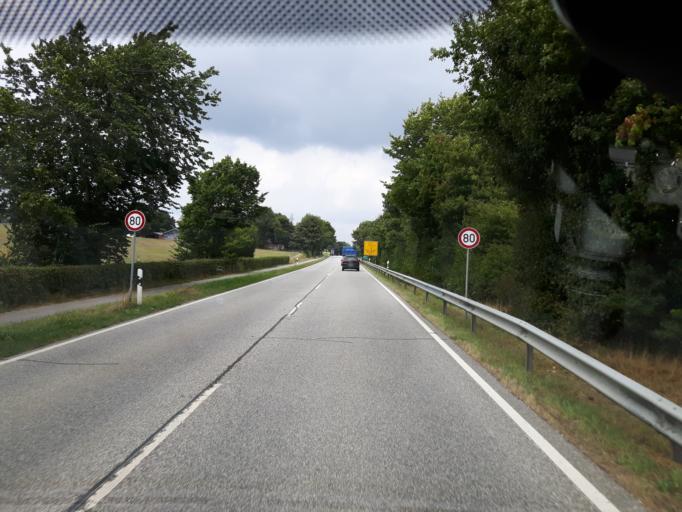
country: DE
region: Schleswig-Holstein
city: Goosefeld
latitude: 54.4261
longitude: 9.8066
